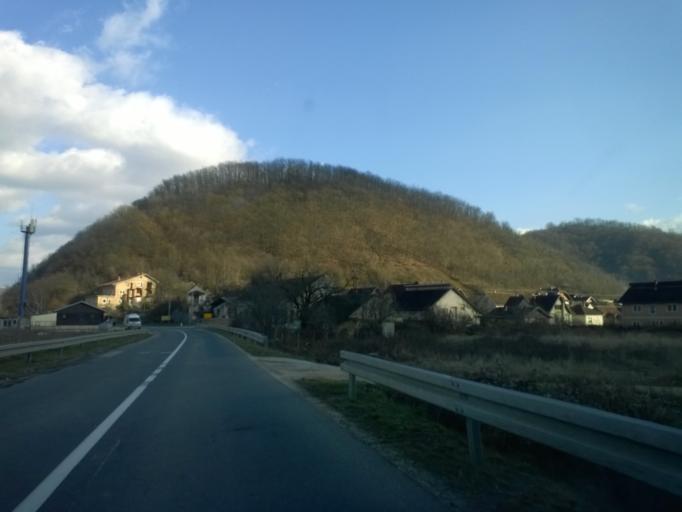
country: RS
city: Radenka
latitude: 44.6563
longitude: 21.7650
